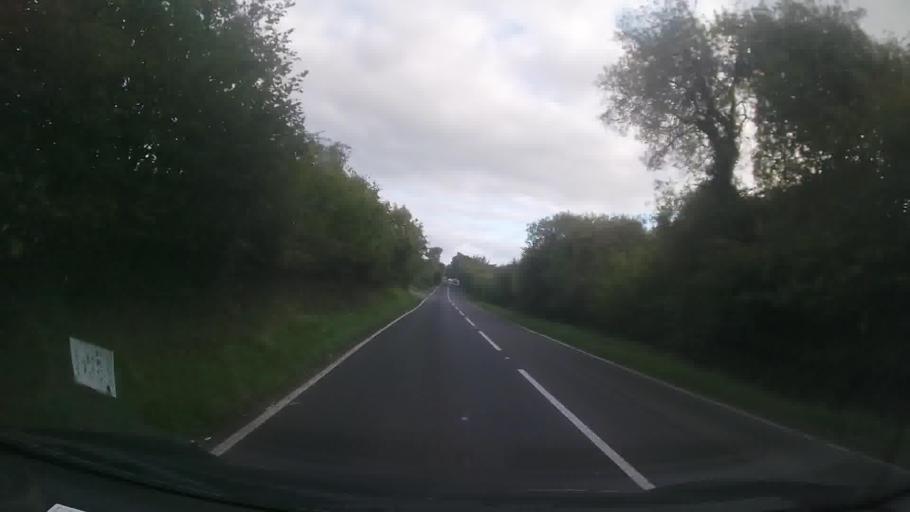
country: GB
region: Wales
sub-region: Pembrokeshire
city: Kilgetty
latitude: 51.7089
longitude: -4.7275
